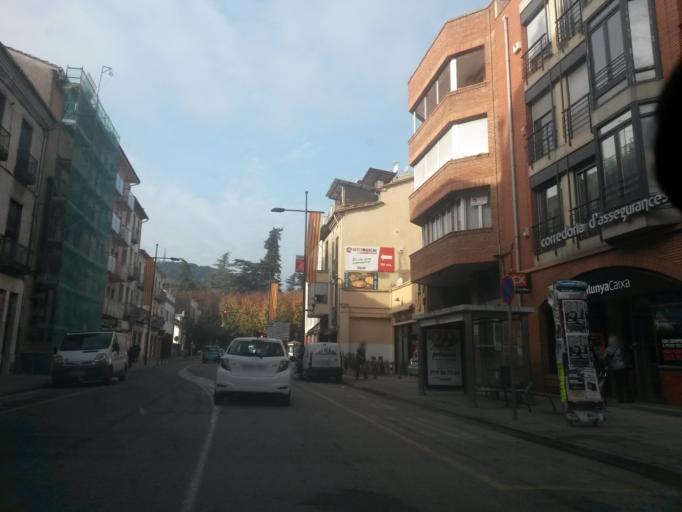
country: ES
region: Catalonia
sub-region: Provincia de Girona
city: Olot
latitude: 42.1808
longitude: 2.4871
